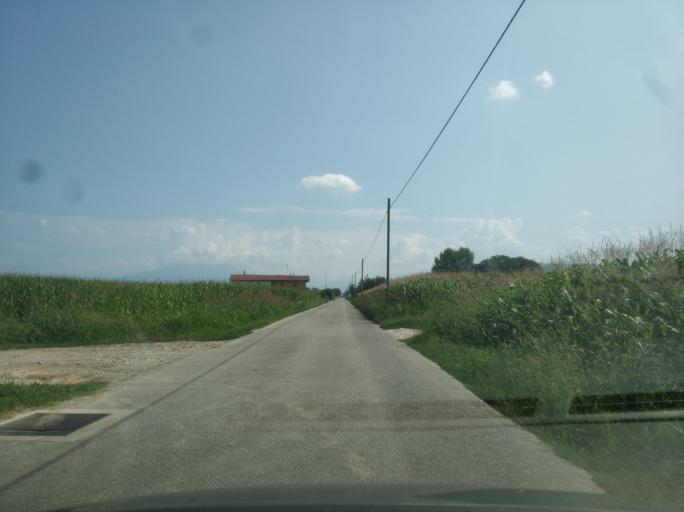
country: IT
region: Piedmont
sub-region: Provincia di Cuneo
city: Caraglio
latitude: 44.4337
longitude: 7.4321
